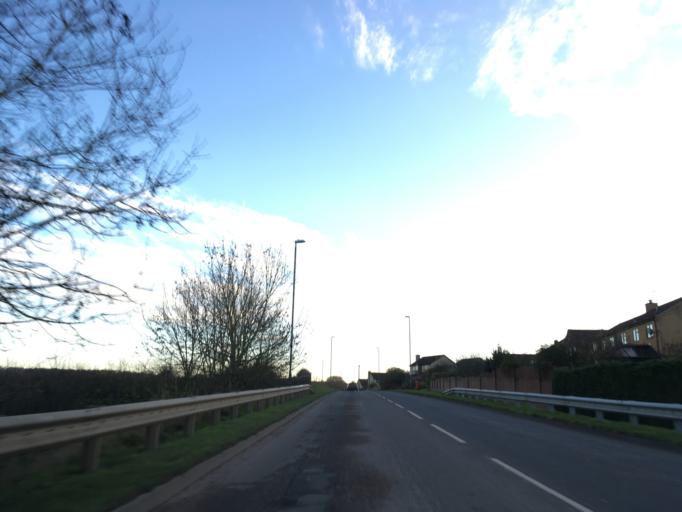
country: GB
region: England
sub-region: South Gloucestershire
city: Thornbury
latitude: 51.6159
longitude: -2.5091
